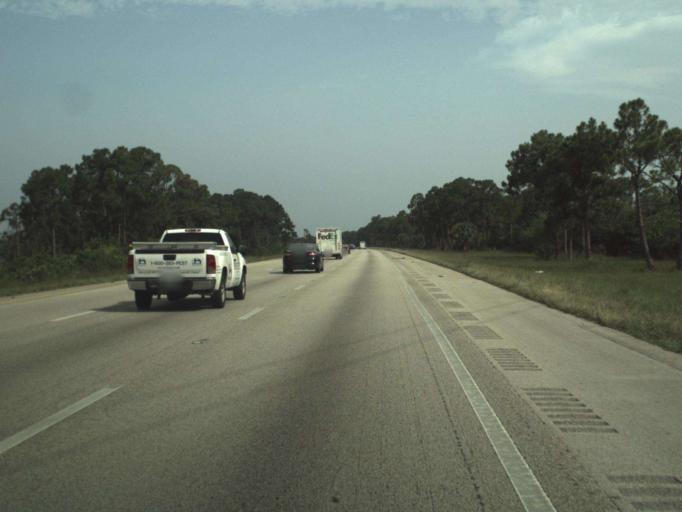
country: US
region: Florida
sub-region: Saint Lucie County
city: Port Saint Lucie
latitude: 27.2458
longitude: -80.4153
